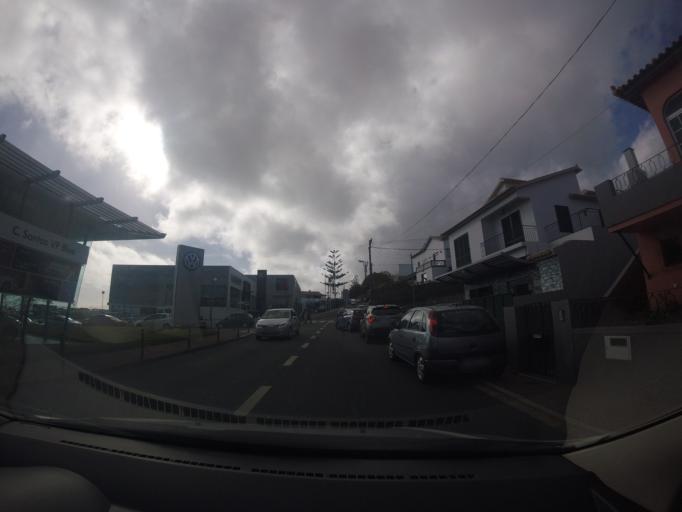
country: PT
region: Madeira
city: Camara de Lobos
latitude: 32.6565
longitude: -16.9437
